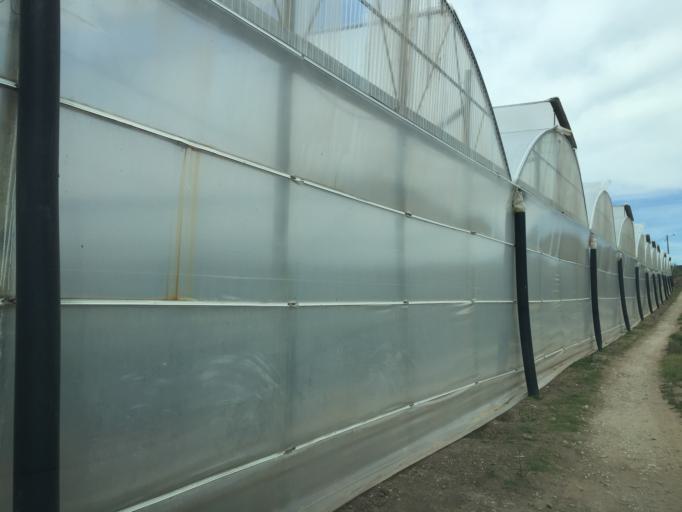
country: PT
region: Lisbon
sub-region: Lourinha
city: Lourinha
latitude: 39.1874
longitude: -9.3448
